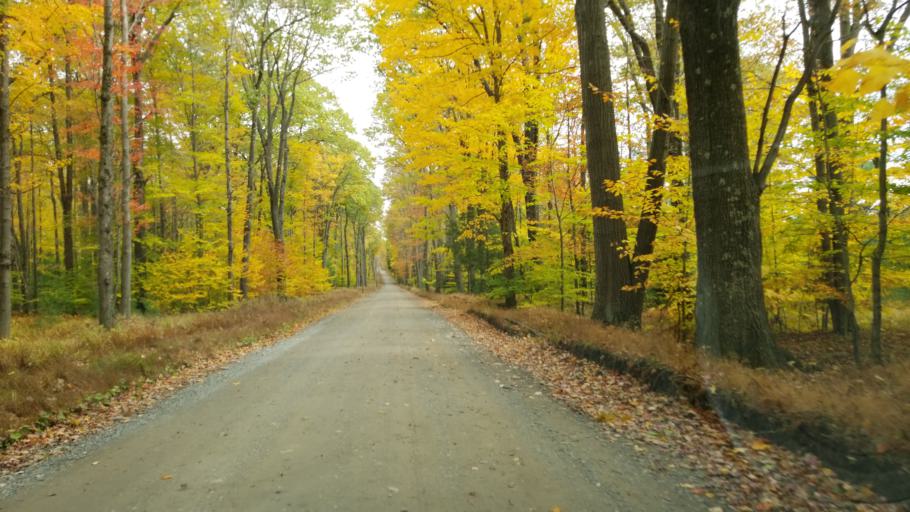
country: US
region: Pennsylvania
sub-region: Clearfield County
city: Shiloh
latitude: 41.1904
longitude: -78.3757
